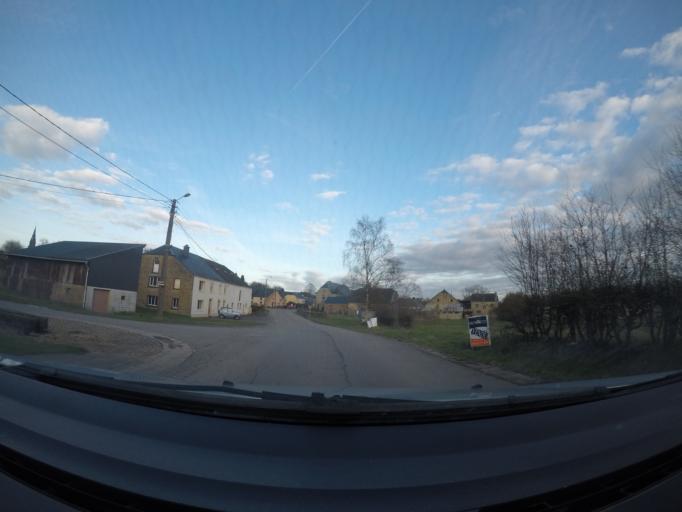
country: BE
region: Wallonia
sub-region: Province du Luxembourg
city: Tintigny
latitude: 49.6987
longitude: 5.5582
